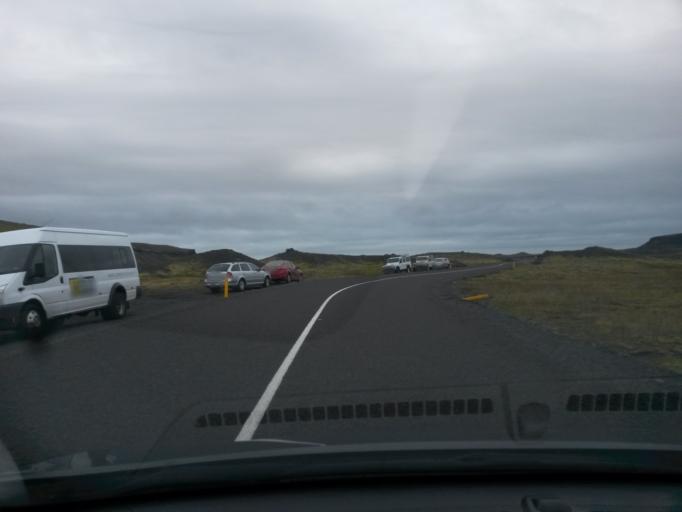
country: IS
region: South
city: Vestmannaeyjar
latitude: 63.5266
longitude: -19.3673
